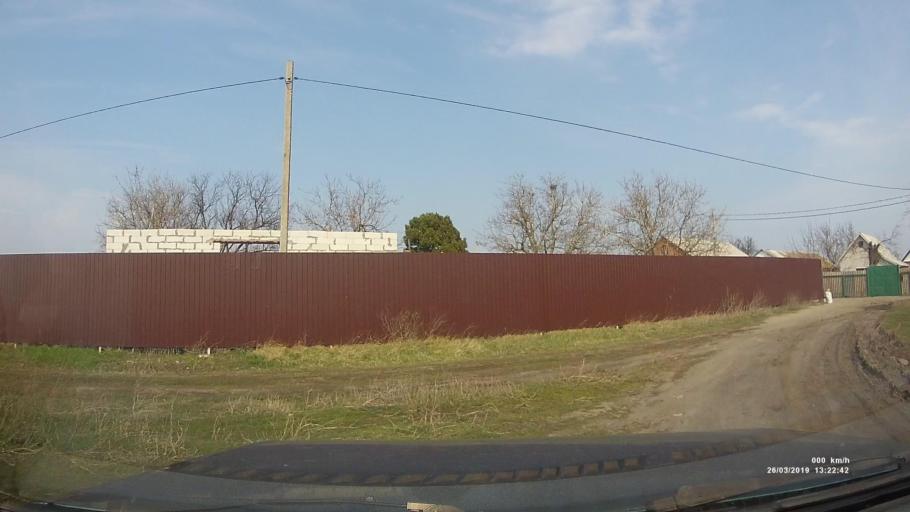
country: RU
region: Rostov
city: Novobessergenovka
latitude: 47.1702
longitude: 38.7671
